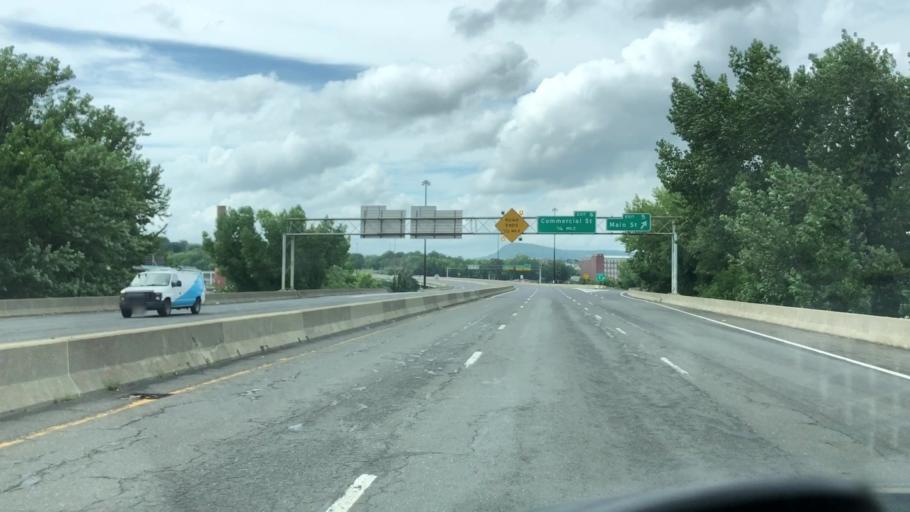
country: US
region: Massachusetts
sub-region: Hampden County
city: North Chicopee
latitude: 42.1905
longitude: -72.6101
